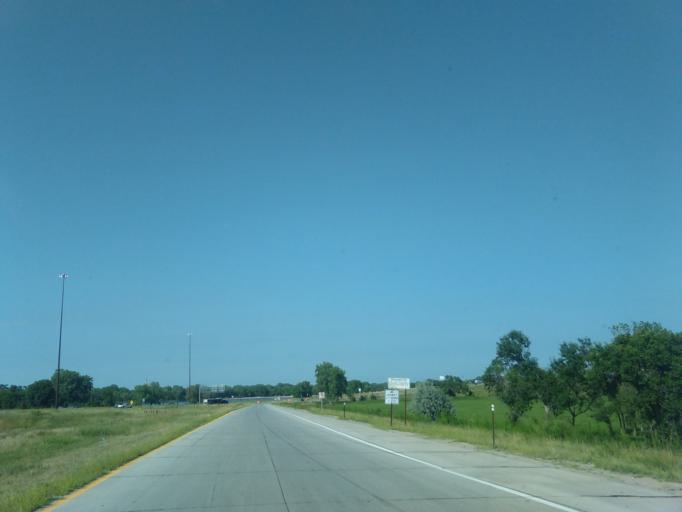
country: US
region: Nebraska
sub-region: Hall County
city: Grand Island
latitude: 40.8183
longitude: -98.3779
